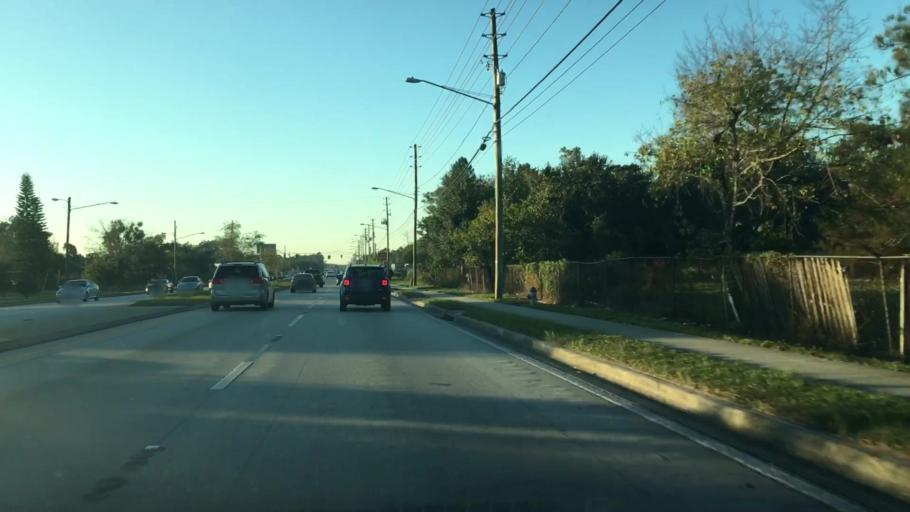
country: US
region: Florida
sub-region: Orange County
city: Conway
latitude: 28.4951
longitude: -81.2855
